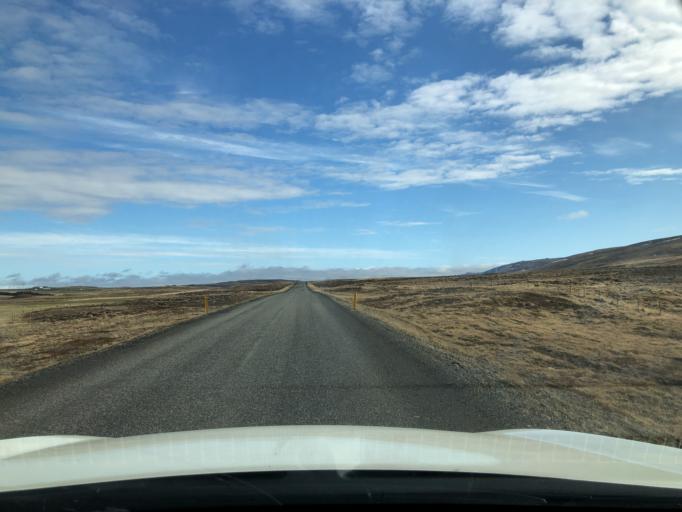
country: IS
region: West
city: Borgarnes
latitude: 65.1010
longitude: -21.7136
